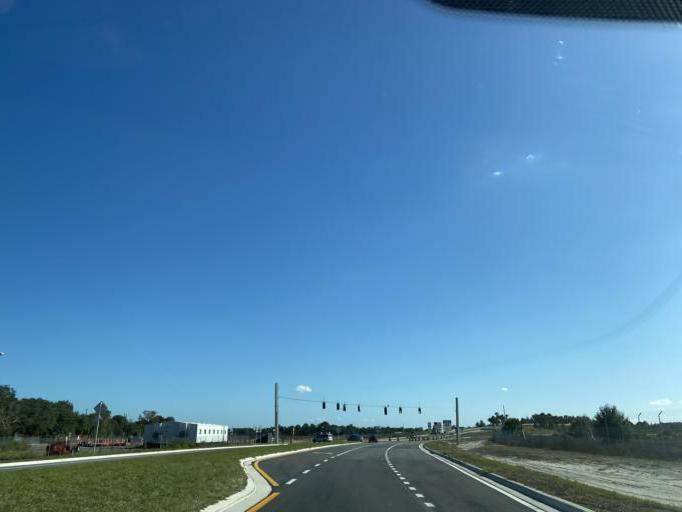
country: US
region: Florida
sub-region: Lake County
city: Mount Plymouth
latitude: 28.8124
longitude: -81.5123
